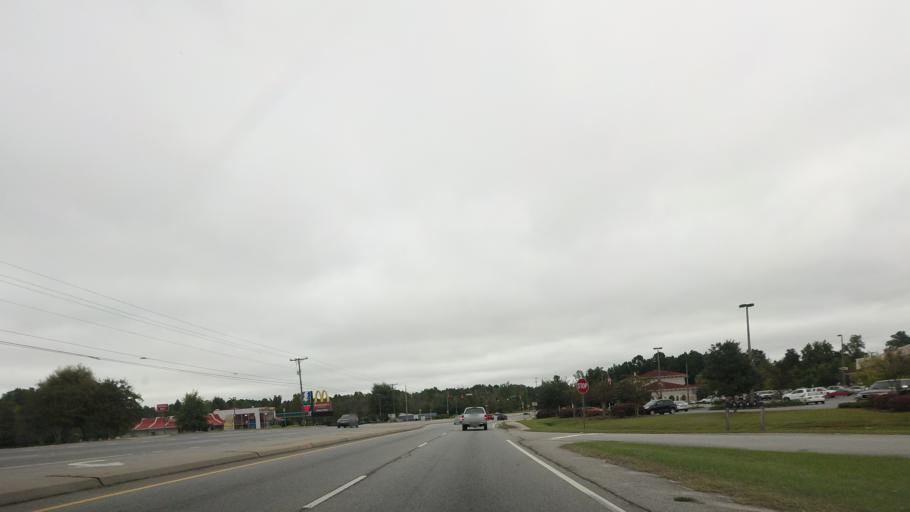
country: US
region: Georgia
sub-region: Lowndes County
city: Valdosta
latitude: 30.9101
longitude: -83.2631
